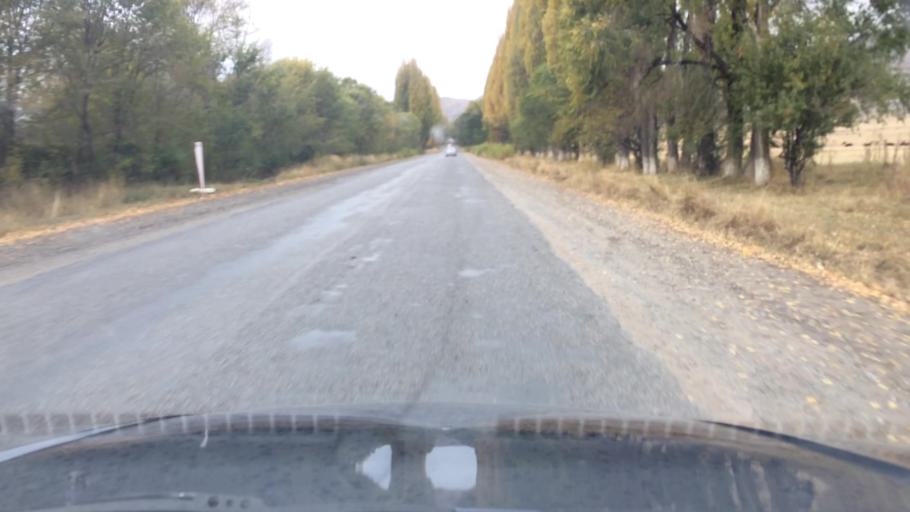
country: KG
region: Ysyk-Koel
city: Pokrovka
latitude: 42.7381
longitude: 77.9214
